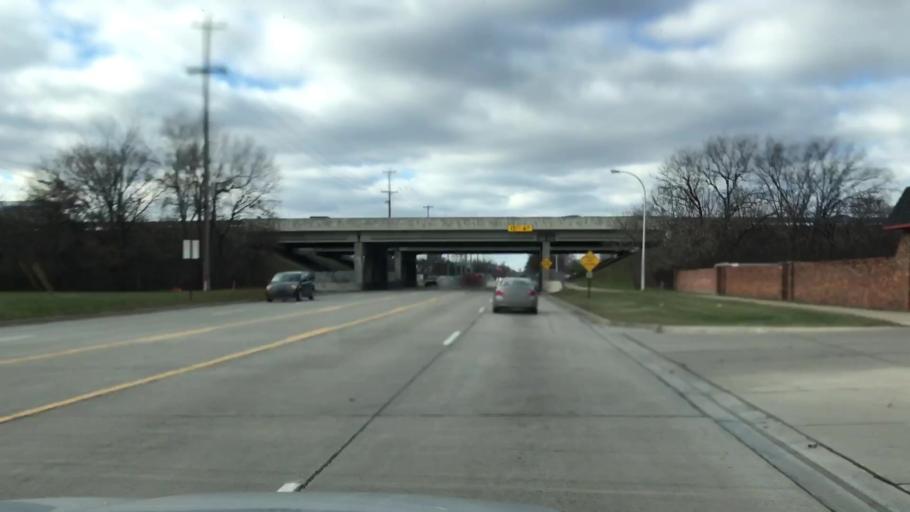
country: US
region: Michigan
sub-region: Oakland County
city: Clawson
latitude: 42.5199
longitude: -83.1142
